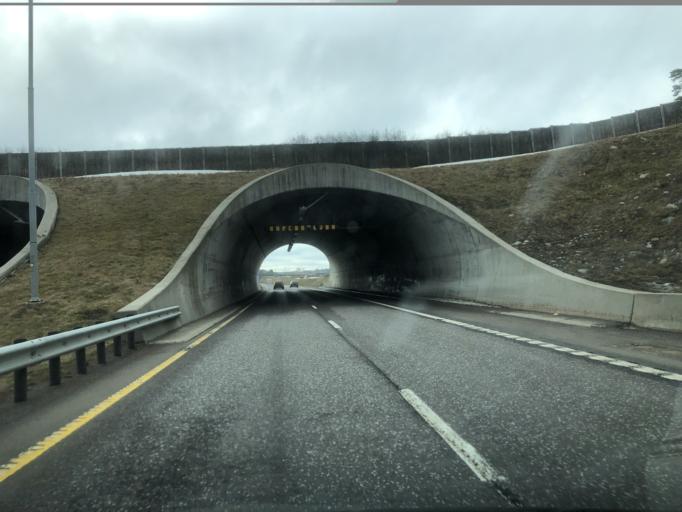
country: NO
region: Vestfold
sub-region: Sandefjord
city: Sandefjord
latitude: 59.1246
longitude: 10.1391
